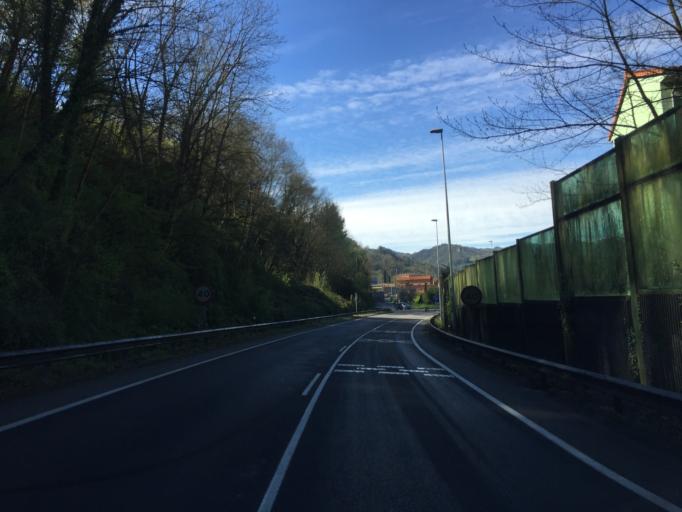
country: ES
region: Asturias
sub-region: Province of Asturias
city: Castandiello
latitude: 43.3548
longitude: -5.9609
